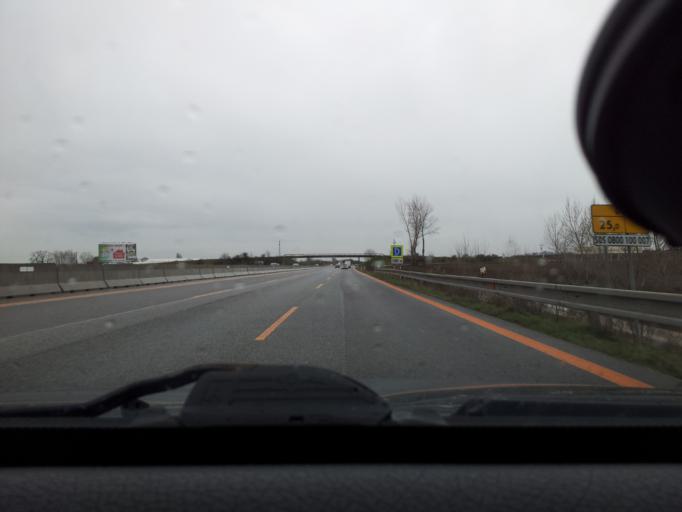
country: SK
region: Bratislavsky
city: Senec
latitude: 48.2263
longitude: 17.3495
